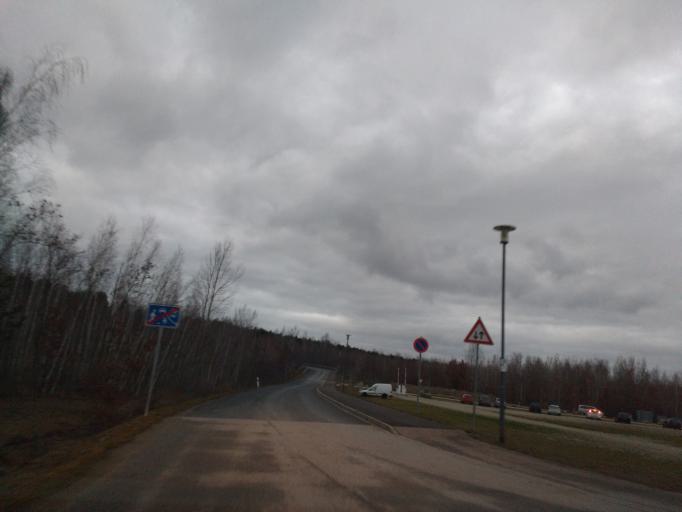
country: DE
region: Saxony-Anhalt
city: Mucheln
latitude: 51.3083
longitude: 11.8092
